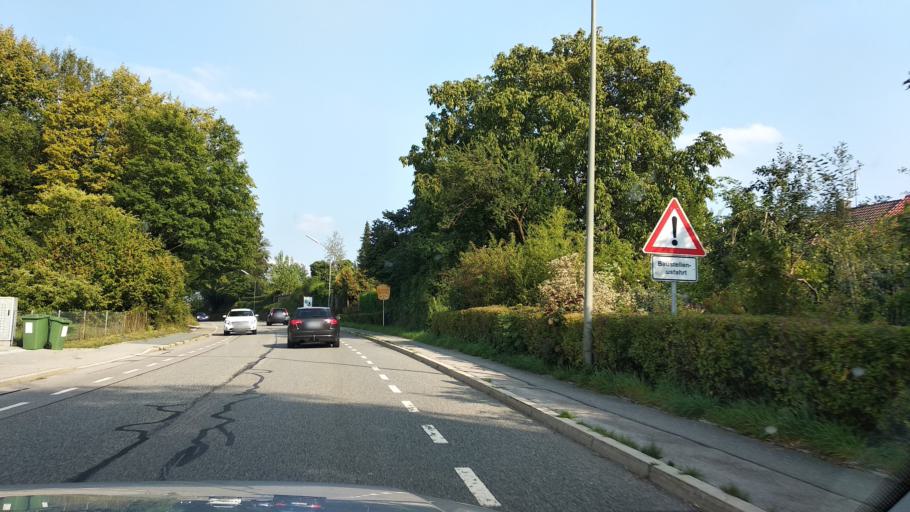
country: DE
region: Bavaria
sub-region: Upper Bavaria
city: Ebersberg
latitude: 48.0756
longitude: 11.9578
